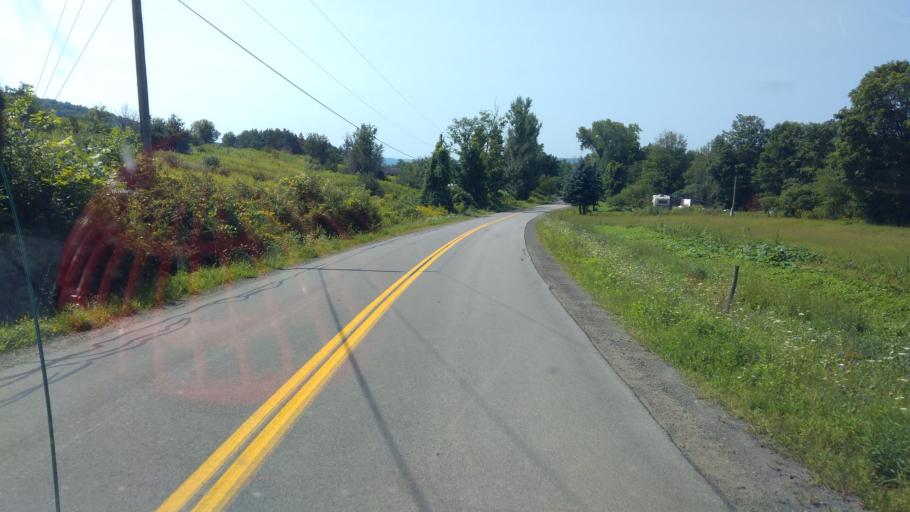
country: US
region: New York
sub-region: Allegany County
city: Belmont
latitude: 42.2691
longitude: -77.9928
